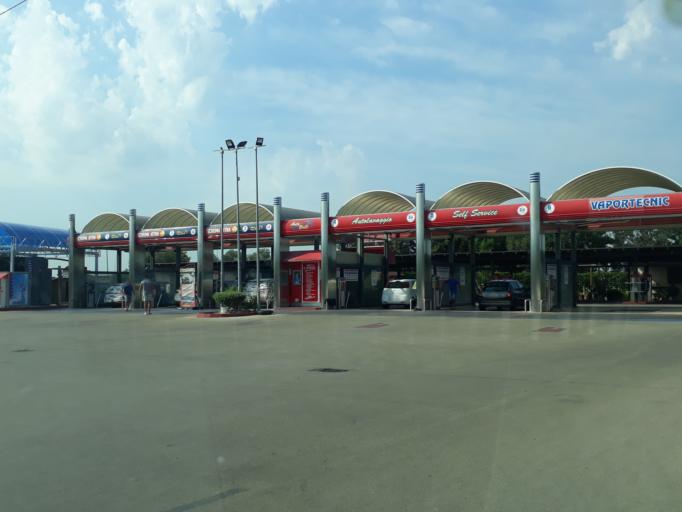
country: IT
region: Apulia
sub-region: Provincia di Brindisi
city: Carovigno
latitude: 40.6875
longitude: 17.6768
